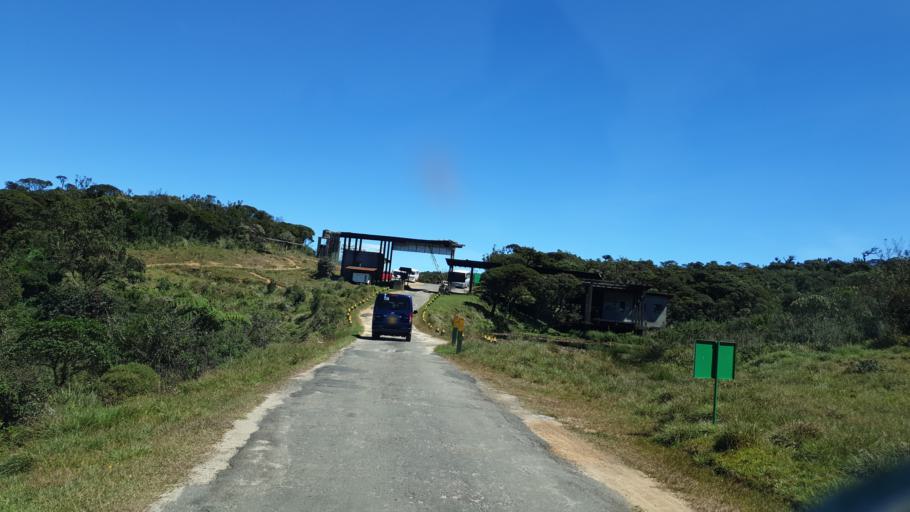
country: LK
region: Central
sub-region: Nuwara Eliya District
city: Nuwara Eliya
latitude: 6.8387
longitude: 80.8115
